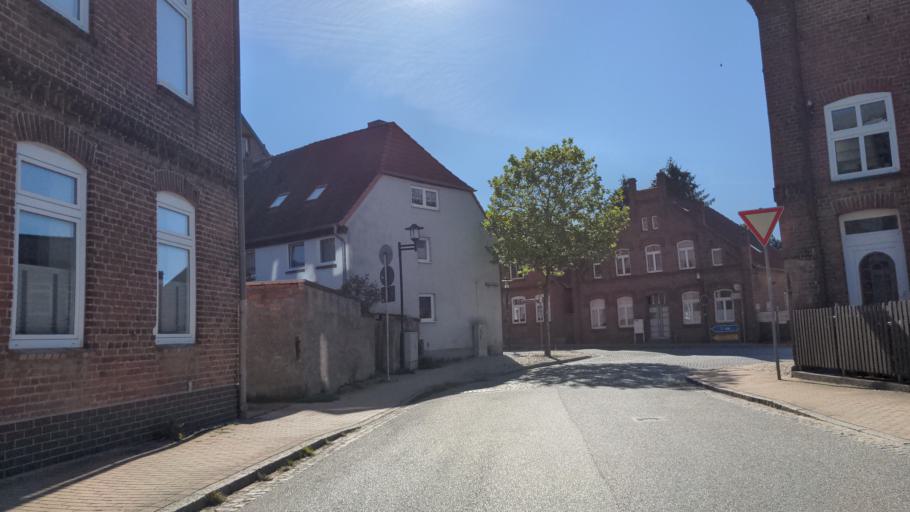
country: DE
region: Mecklenburg-Vorpommern
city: Selmsdorf
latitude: 53.8429
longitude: 10.9292
